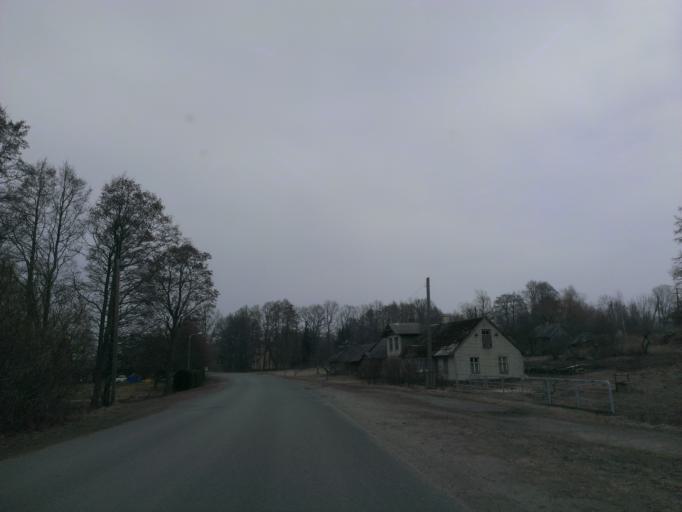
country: LV
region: Salacgrivas
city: Ainazi
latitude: 58.0060
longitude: 24.4448
